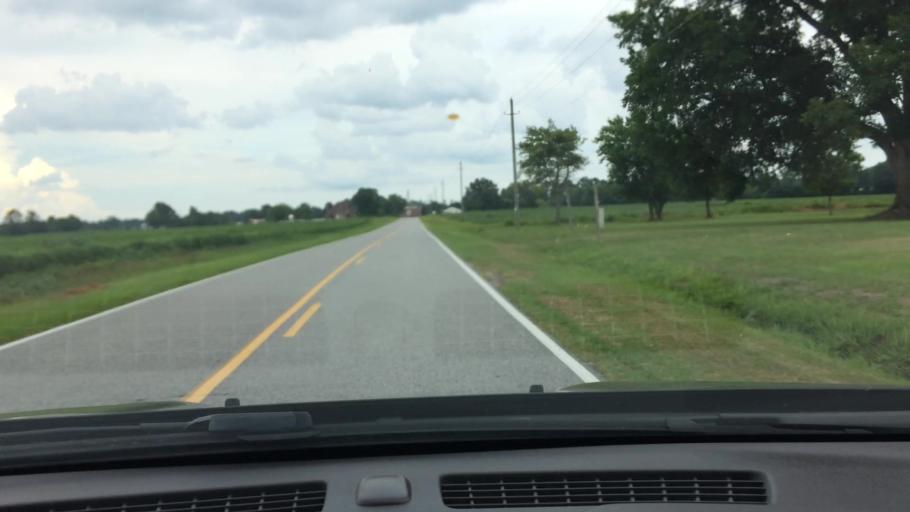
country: US
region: North Carolina
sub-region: Pitt County
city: Ayden
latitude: 35.4331
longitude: -77.4172
